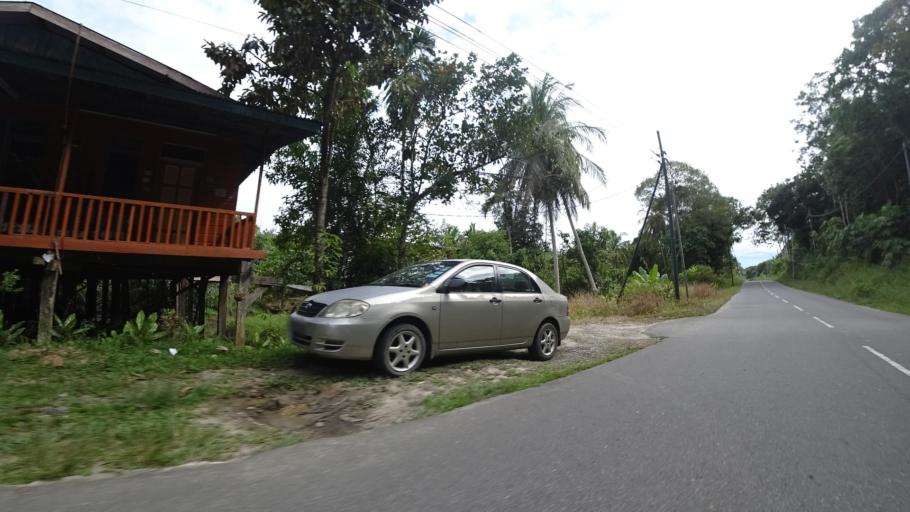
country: BN
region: Brunei and Muara
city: Bandar Seri Begawan
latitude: 4.8451
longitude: 114.9524
